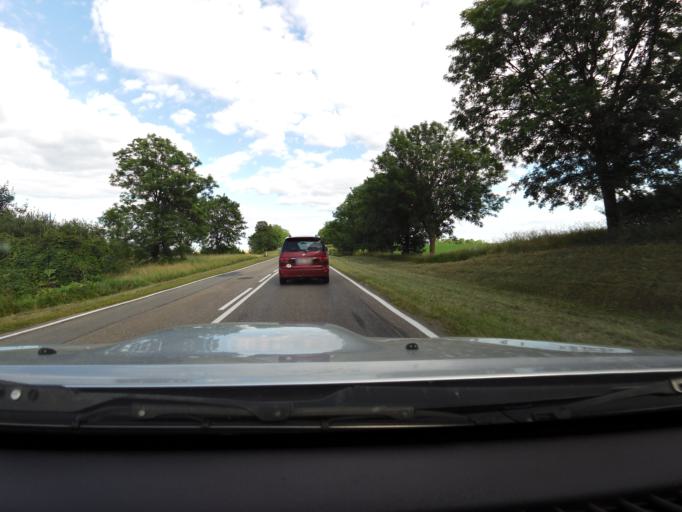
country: PL
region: Podlasie
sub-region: Powiat grajewski
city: Rajgrod
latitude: 53.8610
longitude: 22.7158
